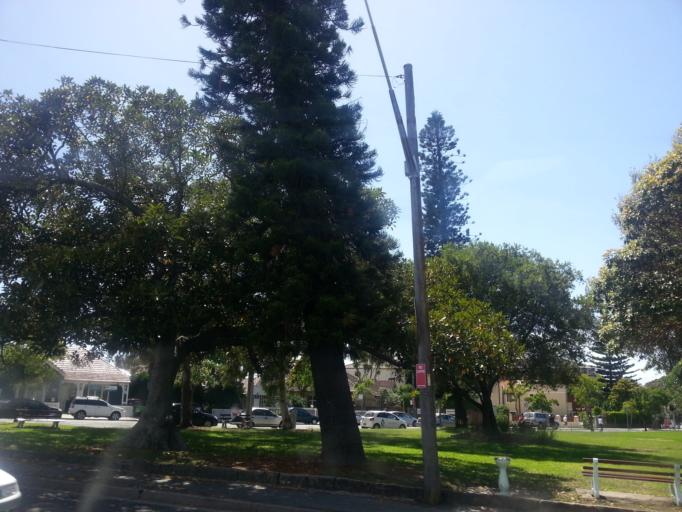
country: AU
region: New South Wales
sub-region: Randwick
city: Randwick
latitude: -33.9177
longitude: 151.2411
